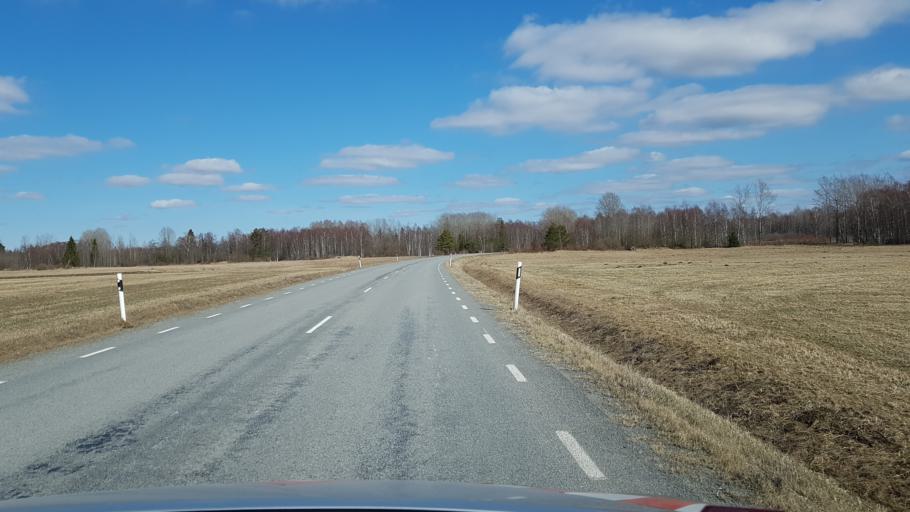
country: EE
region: Laeaene-Virumaa
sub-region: Tapa vald
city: Tapa
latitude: 59.2769
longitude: 25.8770
